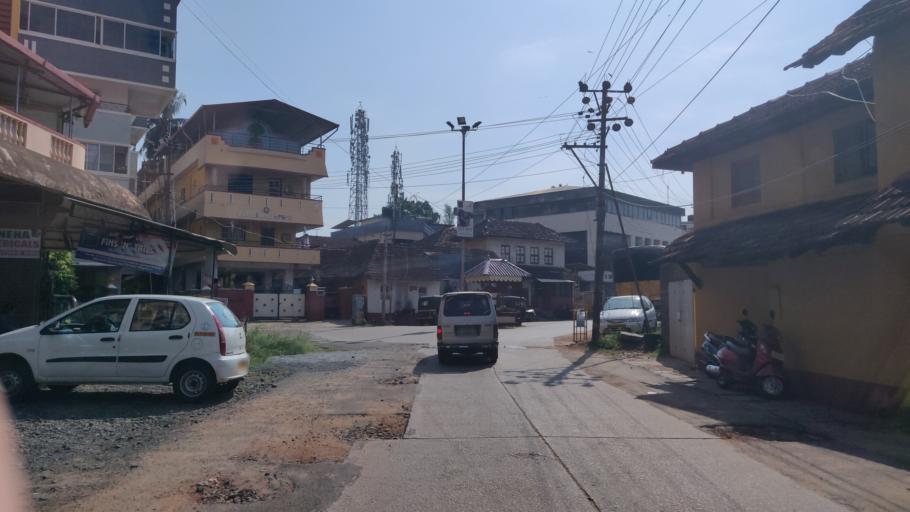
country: IN
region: Karnataka
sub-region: Dakshina Kannada
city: Mangalore
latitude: 12.8730
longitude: 74.8359
